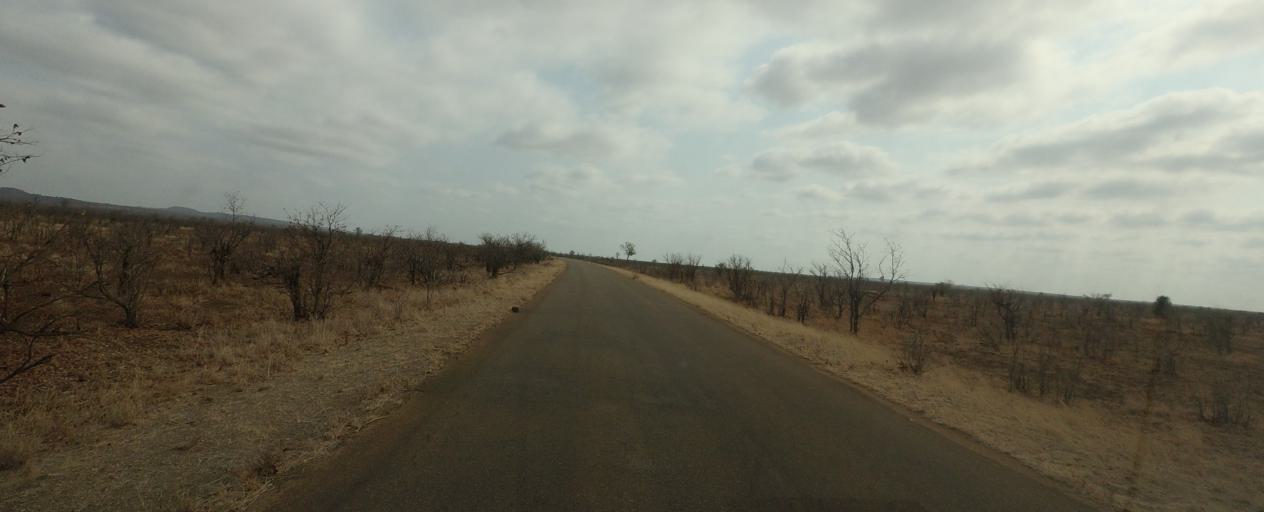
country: ZA
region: Limpopo
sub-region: Vhembe District Municipality
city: Mutale
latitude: -22.6353
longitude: 31.1803
